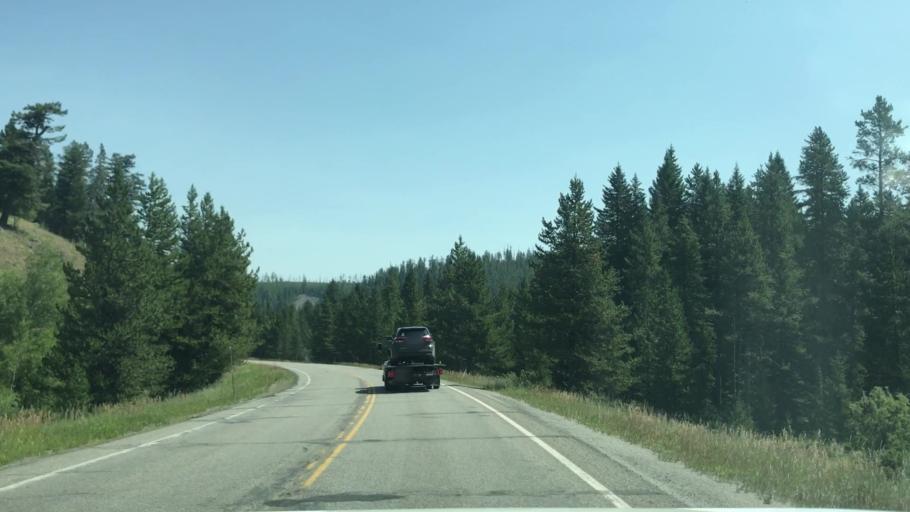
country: US
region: Montana
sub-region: Gallatin County
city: West Yellowstone
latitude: 44.8055
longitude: -111.1027
